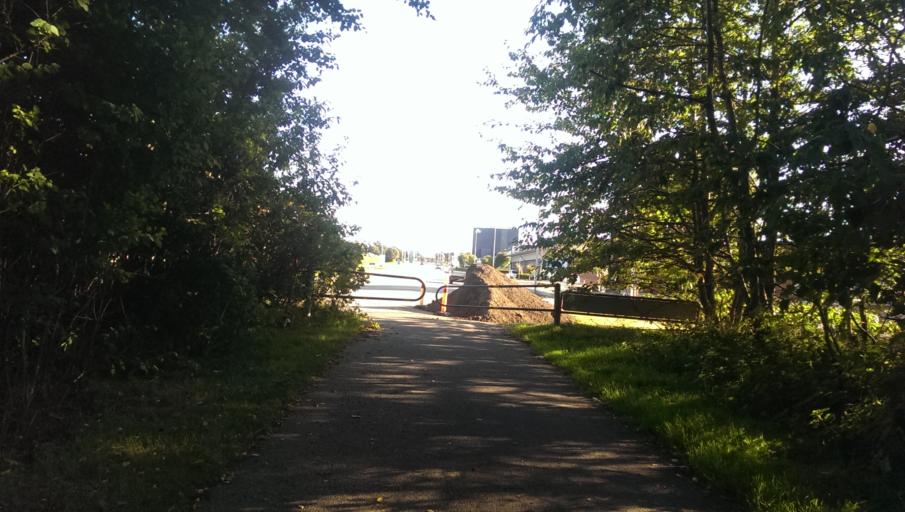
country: DK
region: South Denmark
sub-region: Esbjerg Kommune
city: Esbjerg
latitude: 55.4923
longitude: 8.4746
